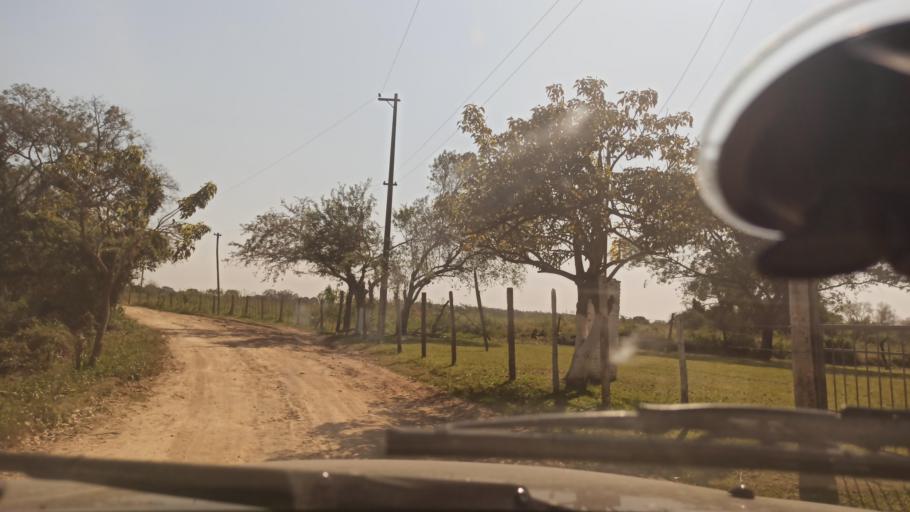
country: AR
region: Formosa
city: Clorinda
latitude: -25.3292
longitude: -57.6857
